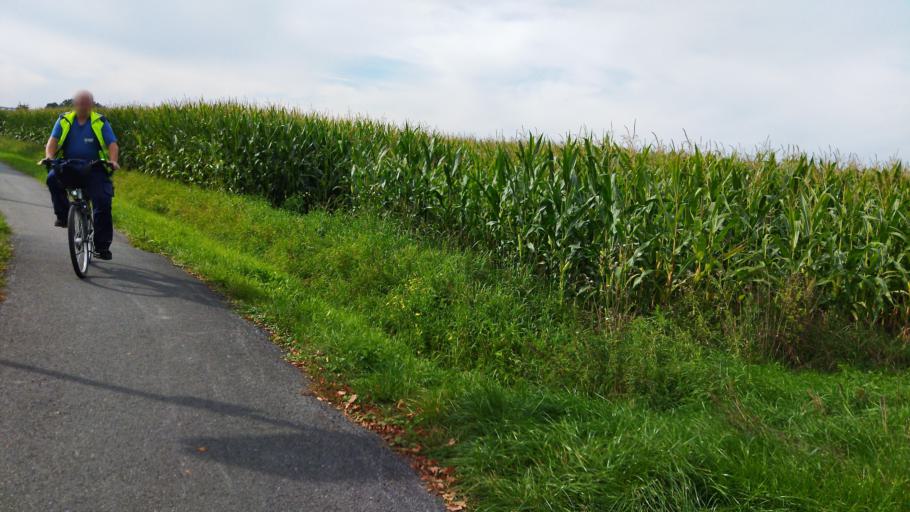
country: DE
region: Lower Saxony
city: Bad Laer
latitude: 52.1015
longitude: 8.0786
